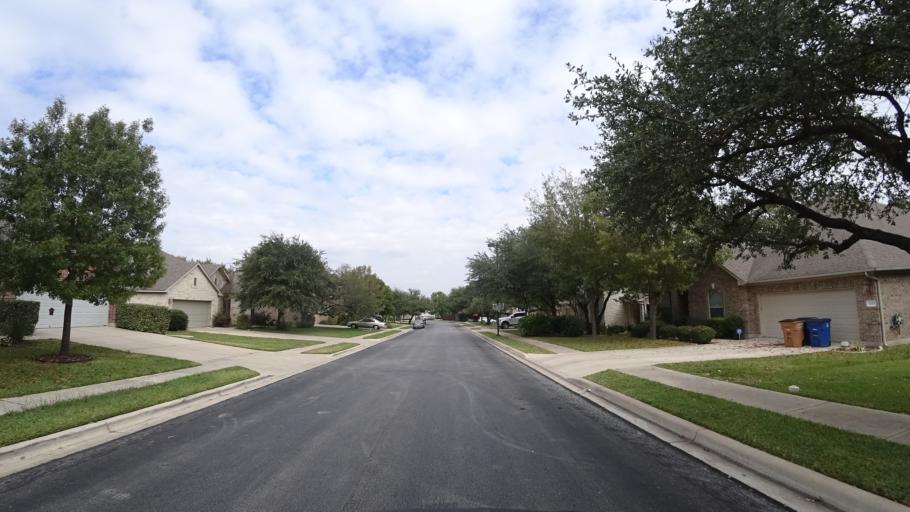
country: US
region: Texas
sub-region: Travis County
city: Shady Hollow
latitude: 30.1903
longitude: -97.8996
